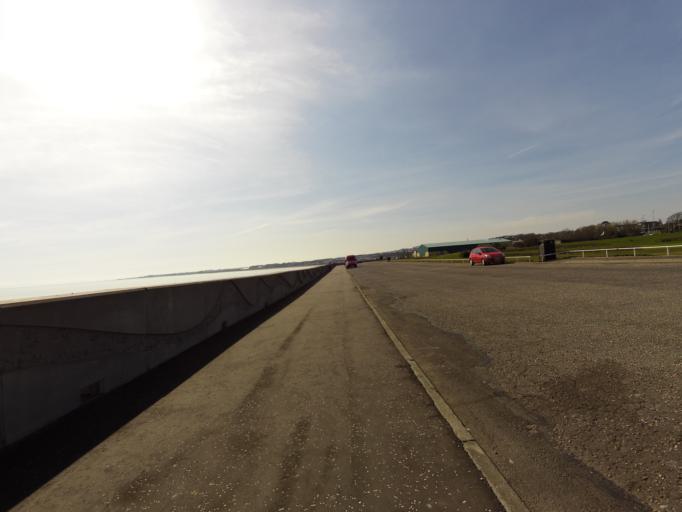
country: GB
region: Scotland
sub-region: Angus
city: Arbroath
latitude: 56.5515
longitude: -2.5935
